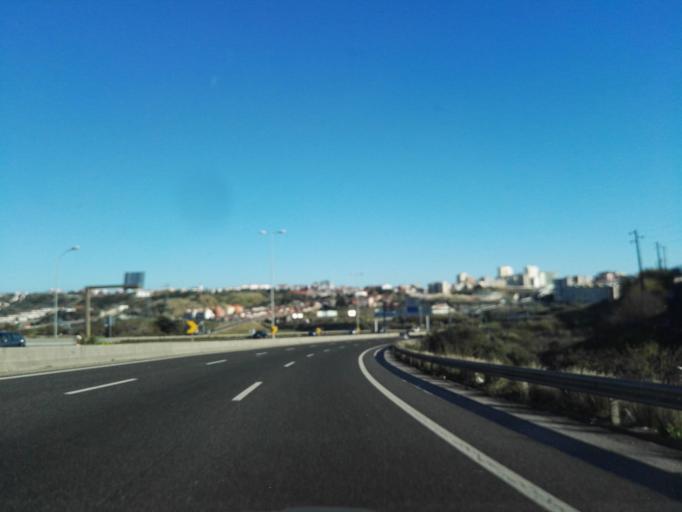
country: PT
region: Lisbon
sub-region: Odivelas
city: Pontinha
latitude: 38.7718
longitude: -9.2139
